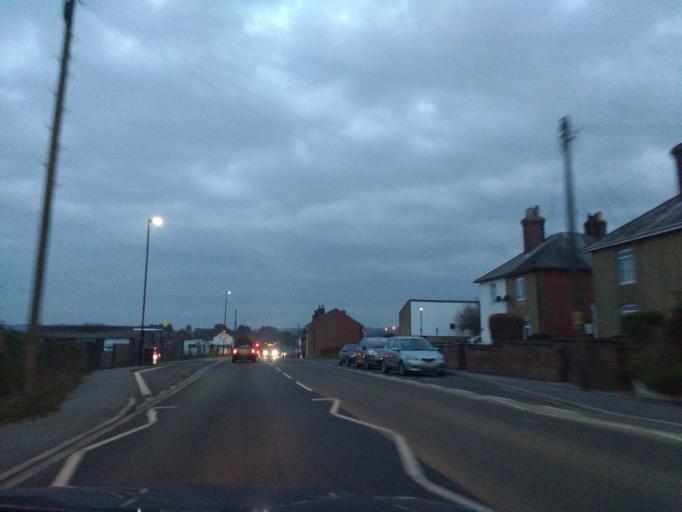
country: GB
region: England
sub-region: Isle of Wight
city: Northwood
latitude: 50.7208
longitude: -1.3044
